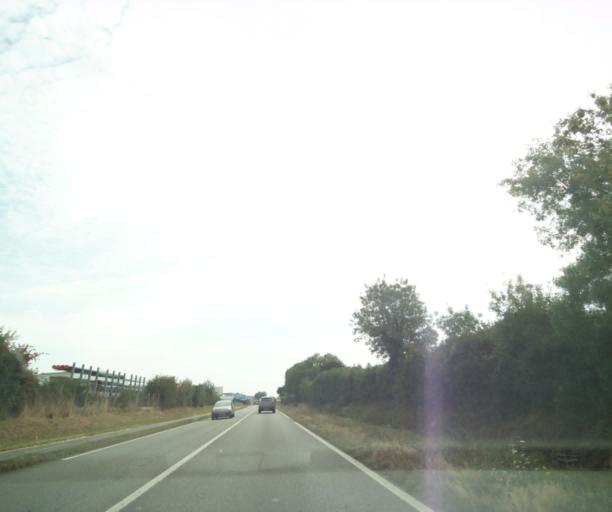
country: FR
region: Pays de la Loire
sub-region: Departement de la Loire-Atlantique
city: Saint-Herblain
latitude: 47.2190
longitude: -1.6514
